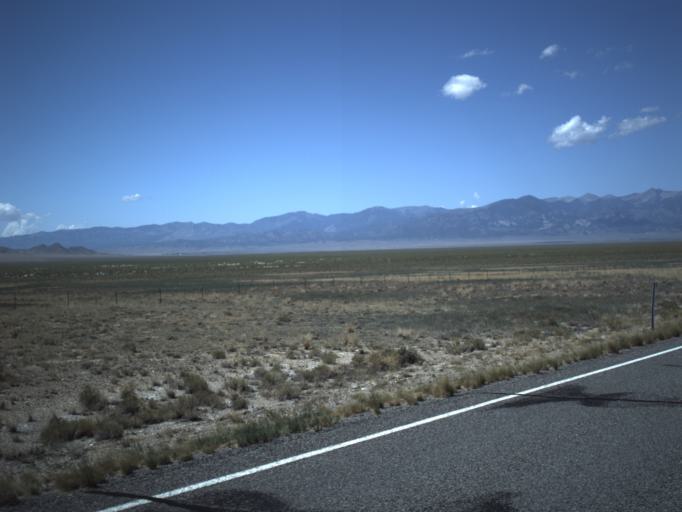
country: US
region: Nevada
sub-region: White Pine County
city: McGill
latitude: 39.0440
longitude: -113.8773
